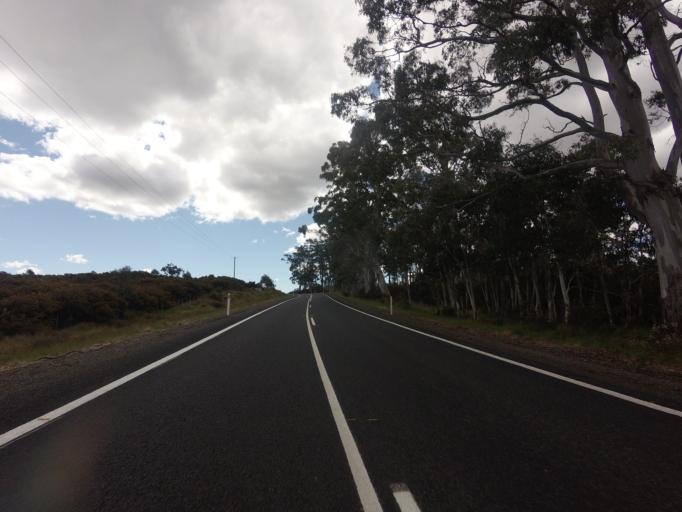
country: AU
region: Tasmania
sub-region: Northern Midlands
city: Evandale
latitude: -41.9826
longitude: 147.6662
